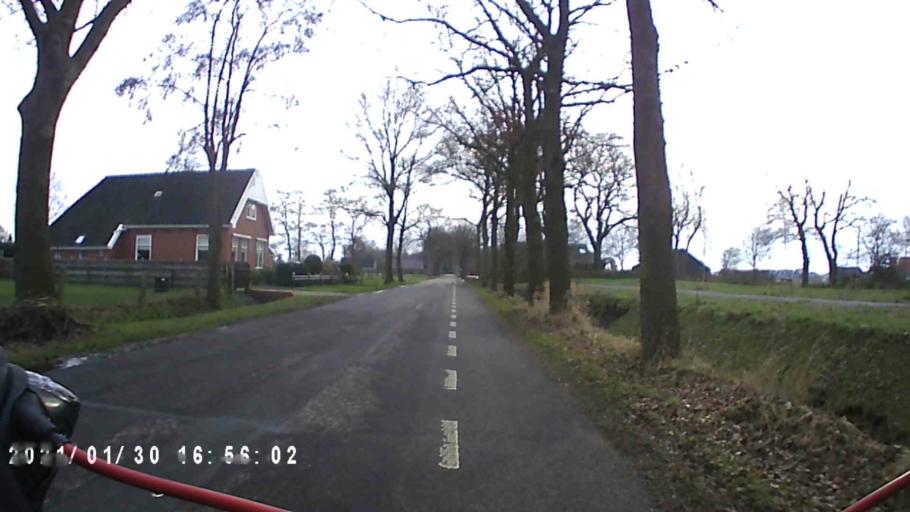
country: NL
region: Groningen
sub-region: Gemeente Leek
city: Leek
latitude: 53.1520
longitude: 6.3817
